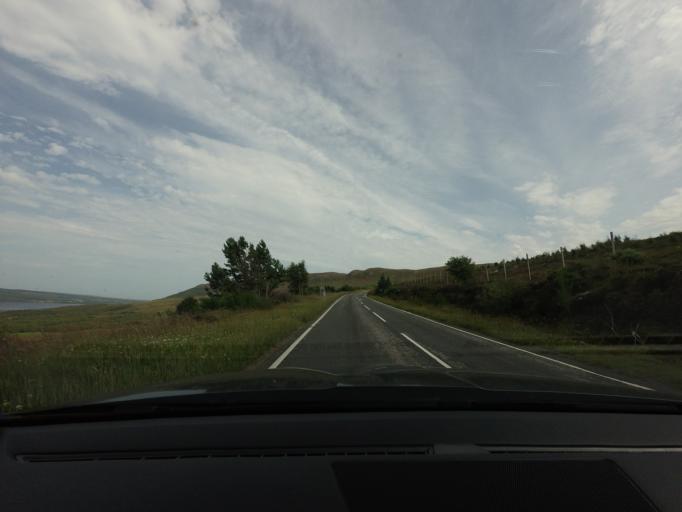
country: GB
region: Scotland
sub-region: Highland
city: Alness
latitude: 57.8428
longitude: -4.2808
